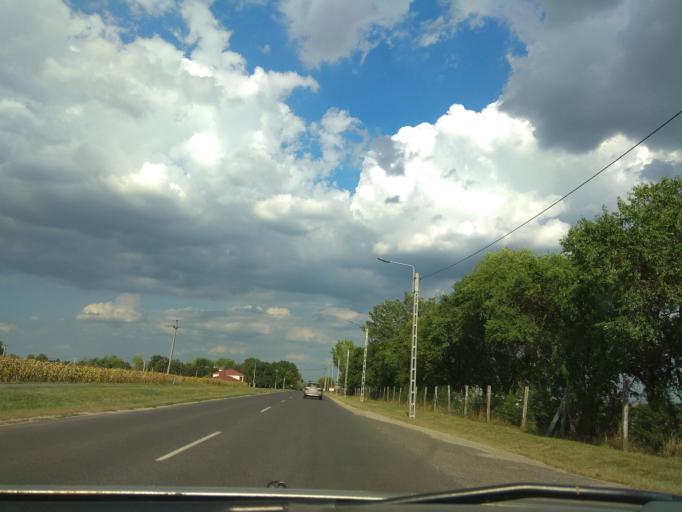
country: HU
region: Borsod-Abauj-Zemplen
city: Mezokovesd
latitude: 47.8005
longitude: 20.5484
